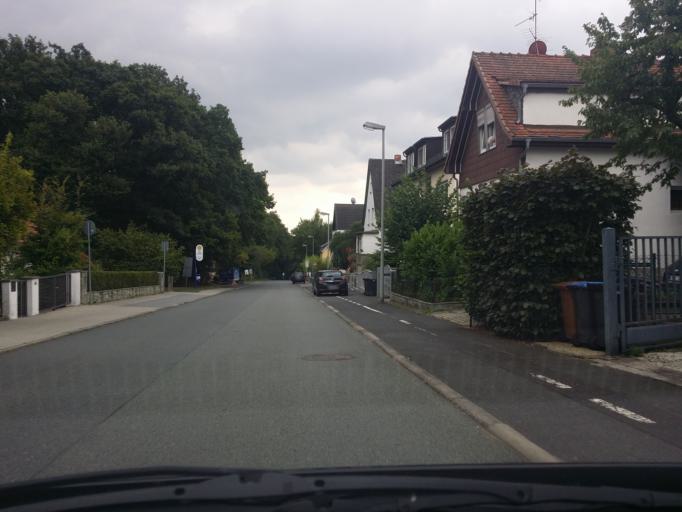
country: DE
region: Hesse
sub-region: Regierungsbezirk Darmstadt
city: Kronberg
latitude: 50.1714
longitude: 8.5036
